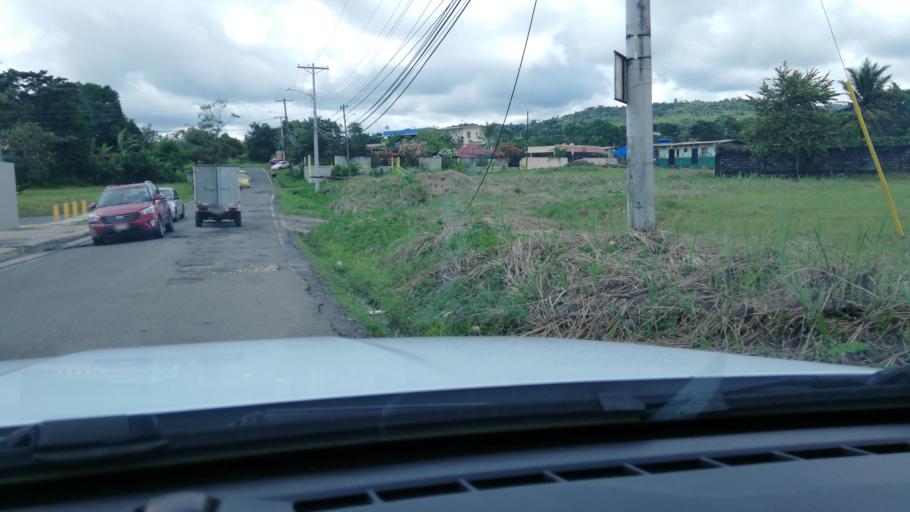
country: PA
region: Panama
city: Tocumen
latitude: 9.1088
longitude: -79.3720
